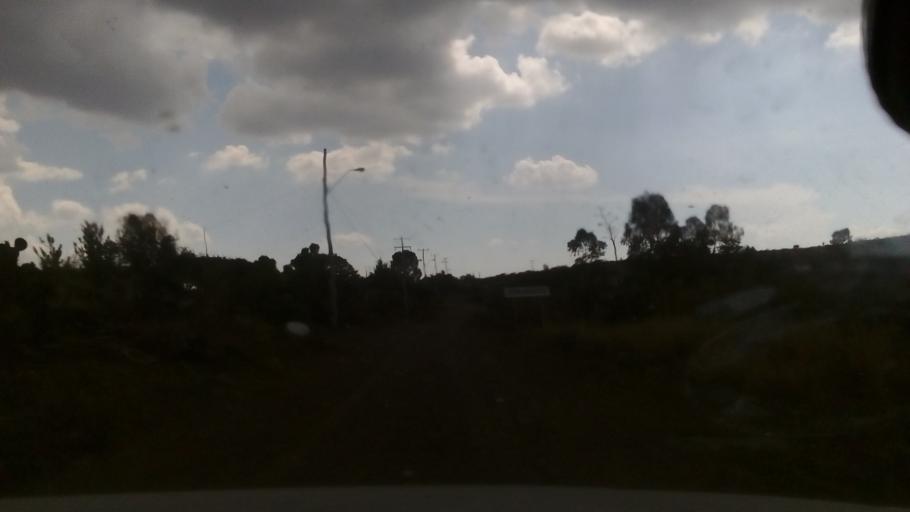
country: MX
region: Guanajuato
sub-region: Silao de la Victoria
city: San Francisco (Banos de Agua Caliente)
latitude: 21.1722
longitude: -101.4153
